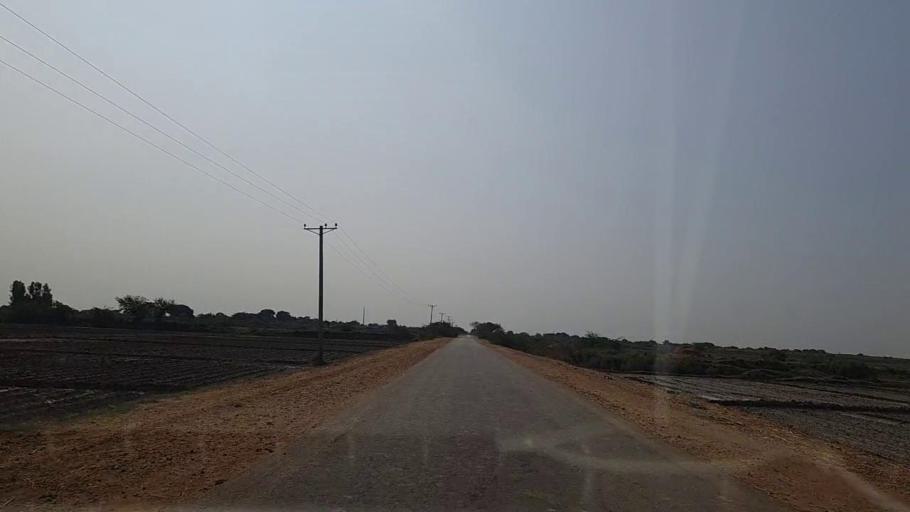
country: PK
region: Sindh
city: Chuhar Jamali
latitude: 24.2802
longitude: 67.9191
